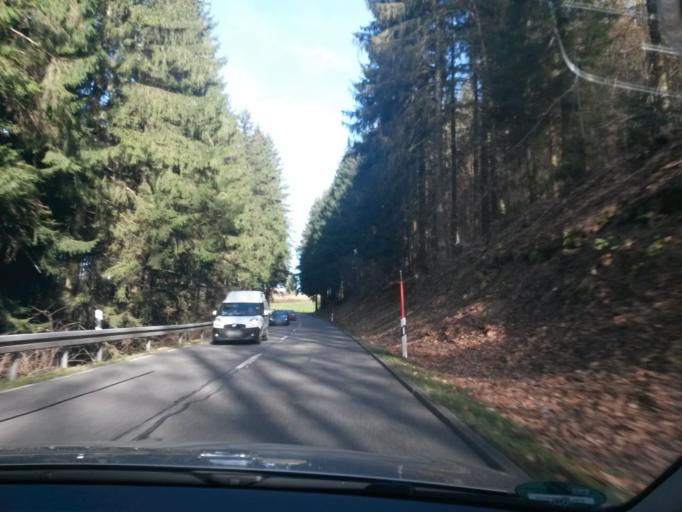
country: DE
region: Baden-Wuerttemberg
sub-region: Freiburg Region
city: Elzach
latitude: 48.2101
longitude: 8.0872
